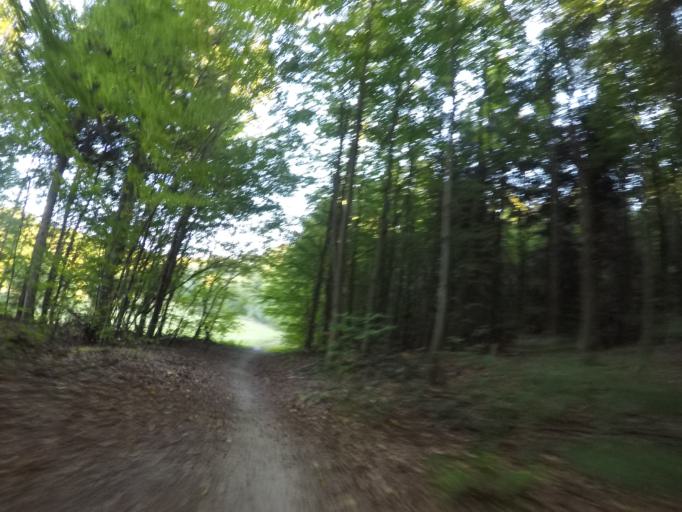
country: SK
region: Kosicky
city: Kosice
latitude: 48.7568
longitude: 21.1570
